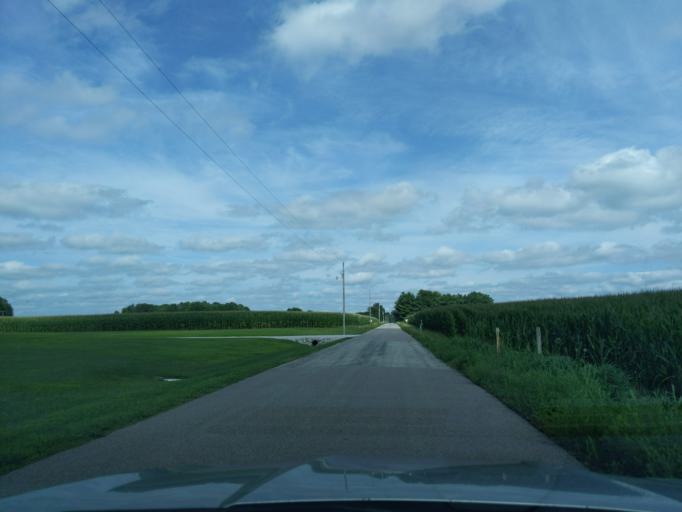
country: US
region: Indiana
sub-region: Decatur County
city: Greensburg
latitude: 39.2344
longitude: -85.4187
